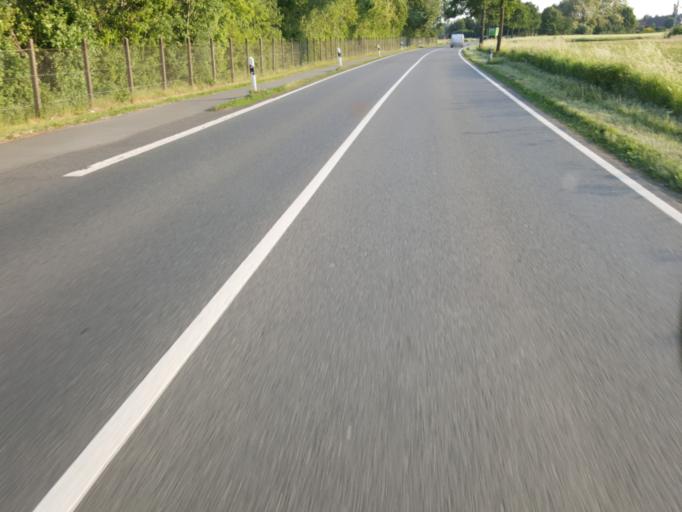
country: DE
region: Lower Saxony
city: Landesbergen
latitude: 52.5470
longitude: 9.1168
